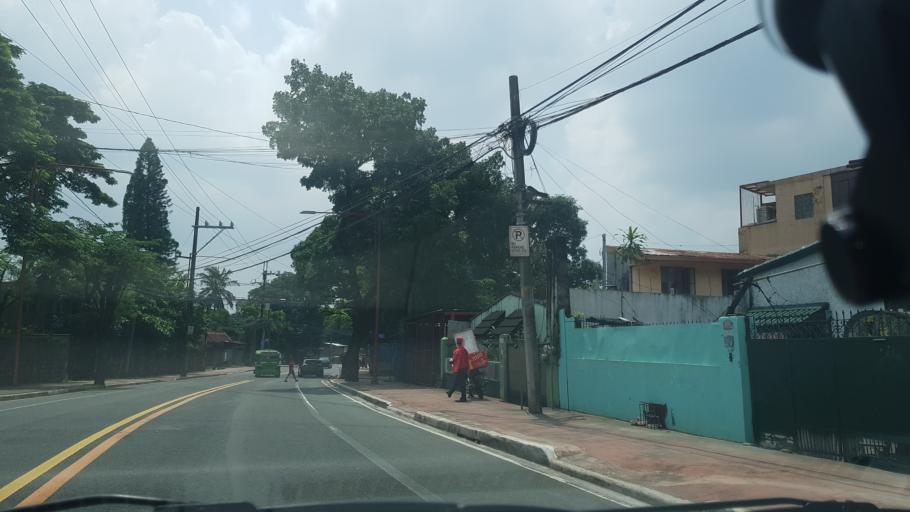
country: PH
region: Calabarzon
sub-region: Province of Rizal
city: Antipolo
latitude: 14.6529
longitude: 121.1139
